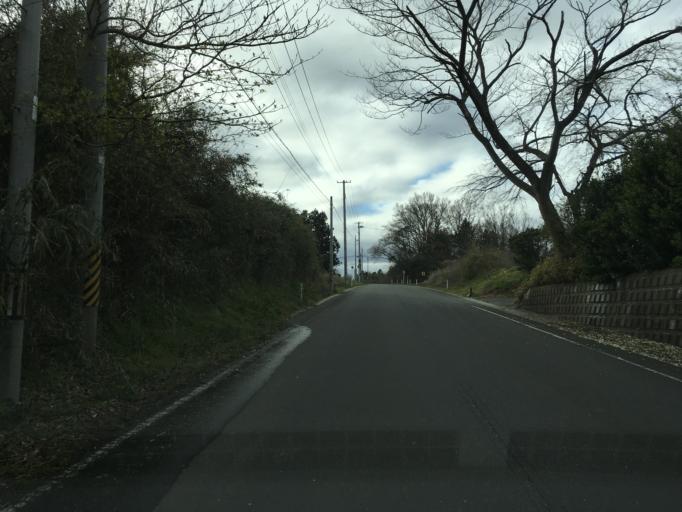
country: JP
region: Iwate
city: Ichinoseki
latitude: 38.7595
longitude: 141.2589
